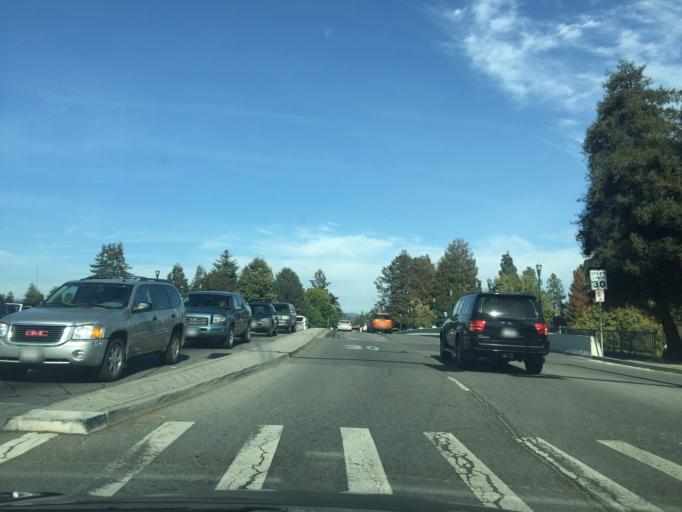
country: US
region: California
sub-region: Santa Cruz County
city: Santa Cruz
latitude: 36.9778
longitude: -122.0253
